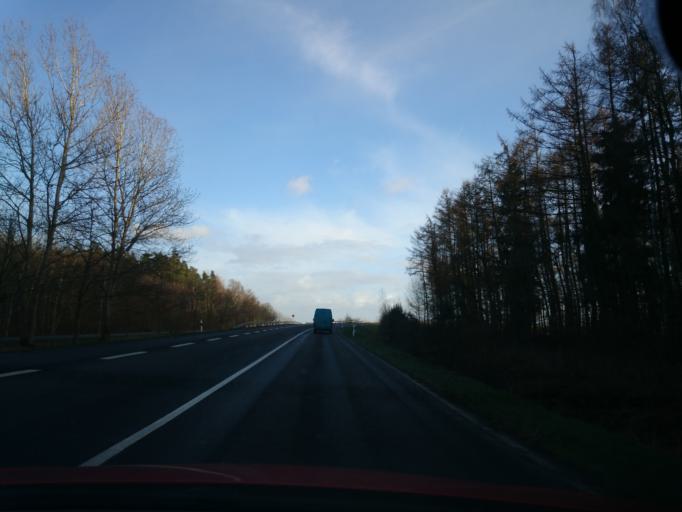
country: DE
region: Mecklenburg-Vorpommern
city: Mesekenhagen
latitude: 54.1234
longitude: 13.3550
